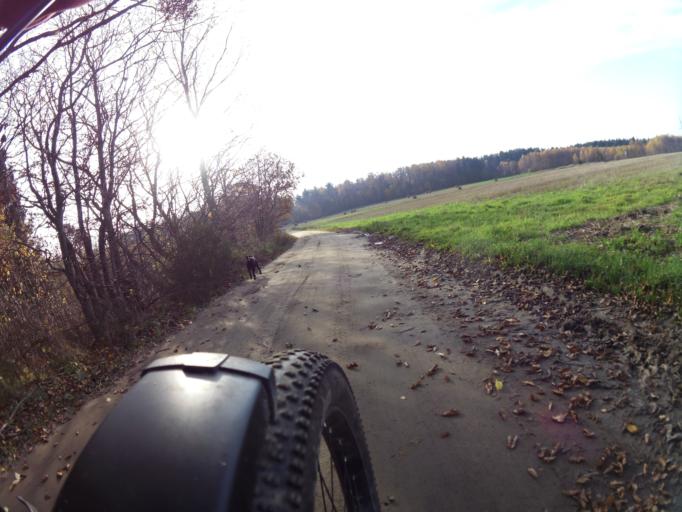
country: PL
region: Pomeranian Voivodeship
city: Strzelno
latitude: 54.7443
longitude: 18.2849
